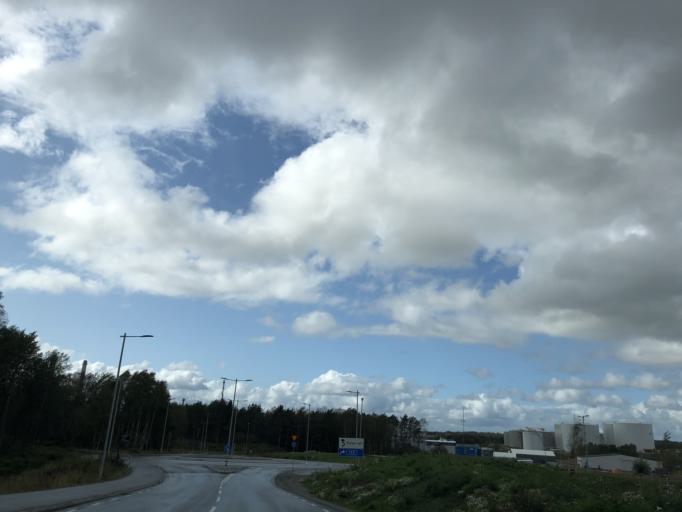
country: SE
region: Vaestra Goetaland
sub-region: Goteborg
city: Torslanda
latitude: 57.7087
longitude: 11.8384
